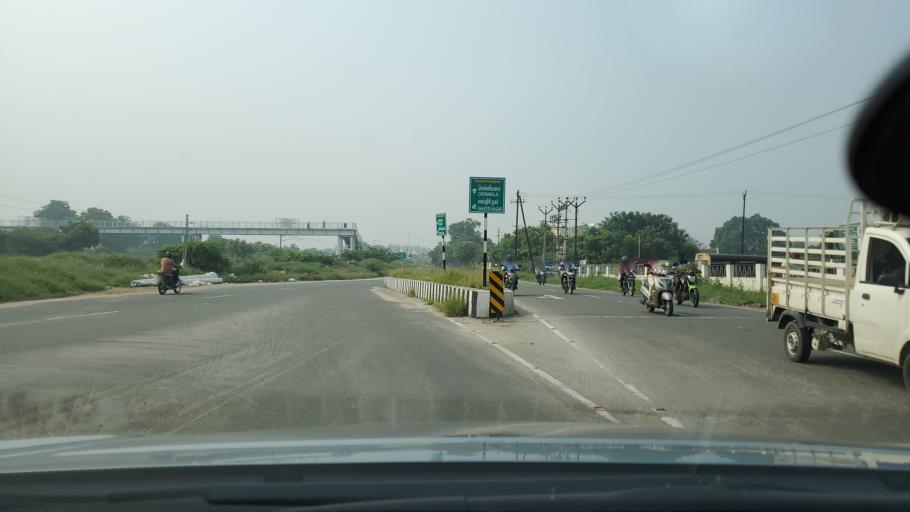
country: IN
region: Tamil Nadu
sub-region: Erode
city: Erode
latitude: 11.3173
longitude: 77.7128
